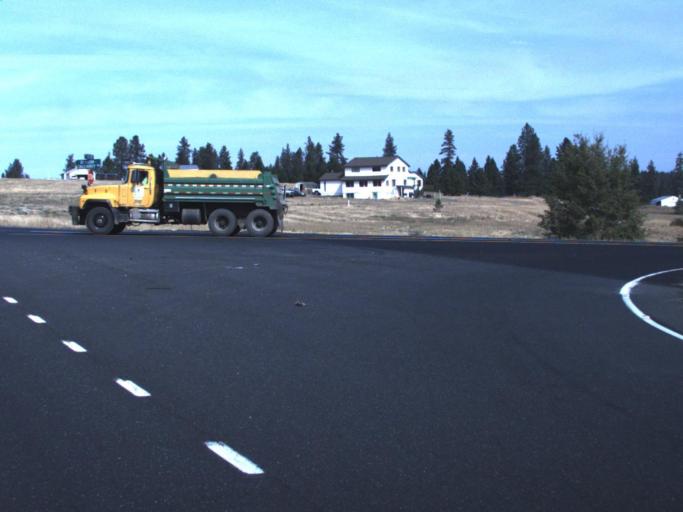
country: US
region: Washington
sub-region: Spokane County
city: Deer Park
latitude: 47.9034
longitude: -117.4395
